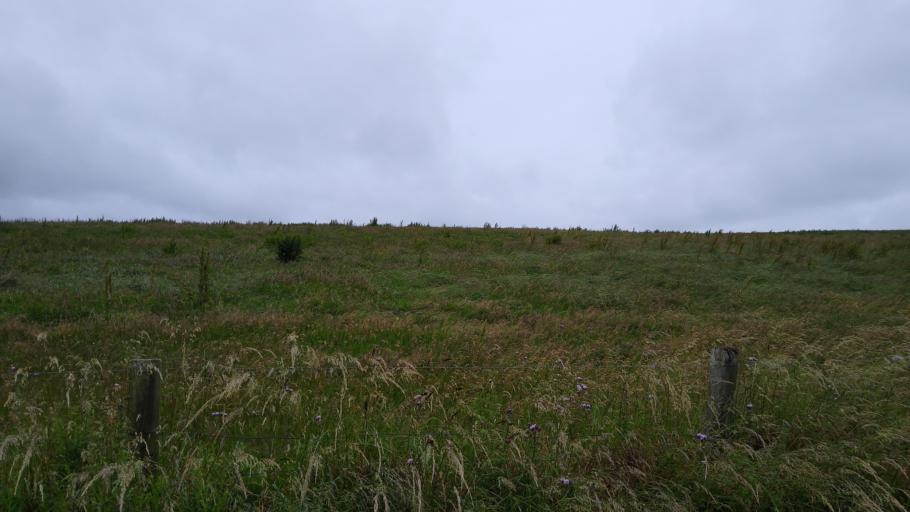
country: GB
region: England
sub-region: Cumbria
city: Flimby
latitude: 54.6966
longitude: -3.5094
